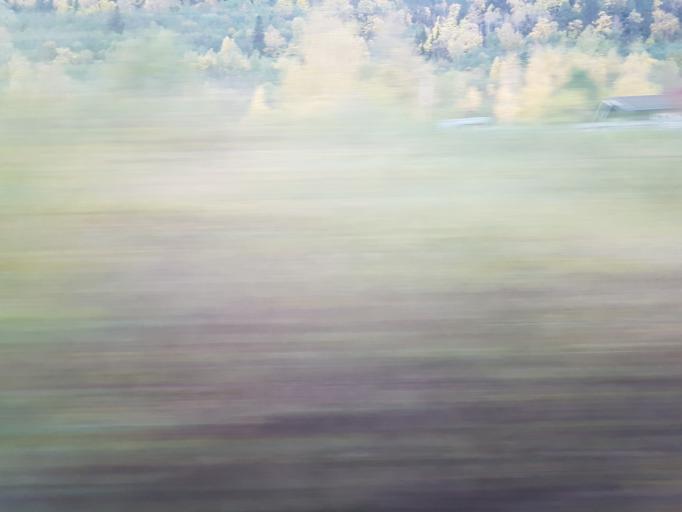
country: NO
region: Oppland
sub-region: Sel
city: Otta
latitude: 61.8395
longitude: 9.4715
